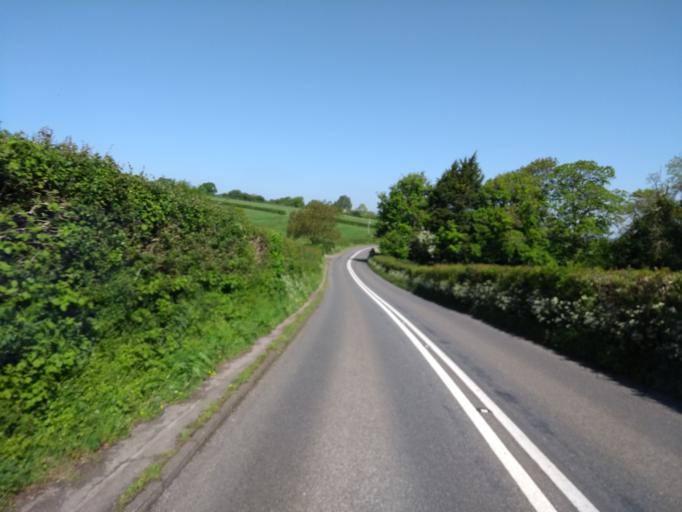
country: GB
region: England
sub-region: Somerset
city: Chard
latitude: 50.8593
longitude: -2.9582
